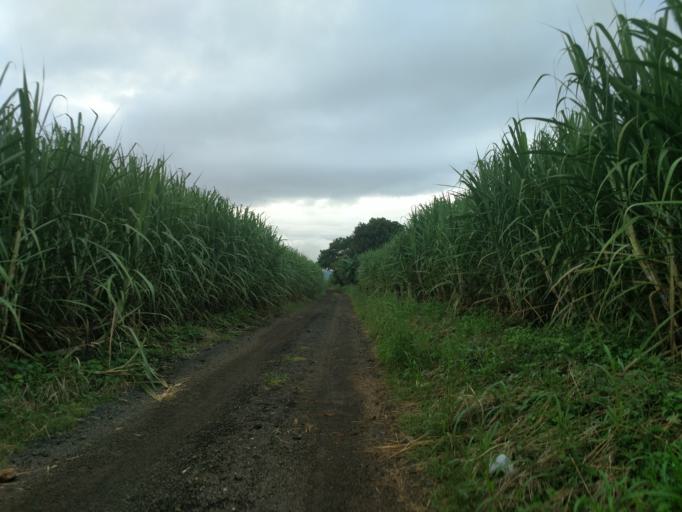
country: MX
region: Nayarit
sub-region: Tepic
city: La Corregidora
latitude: 21.4698
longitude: -104.8016
